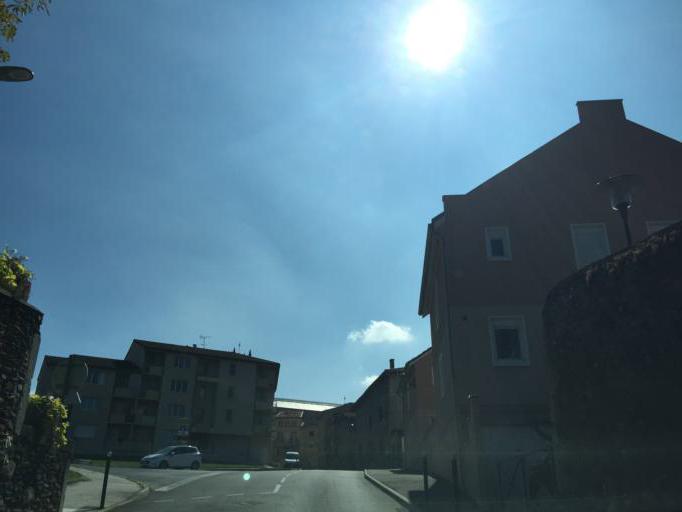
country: FR
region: Rhone-Alpes
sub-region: Departement de la Loire
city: Saint-Paul-en-Jarez
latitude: 45.4845
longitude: 4.5741
